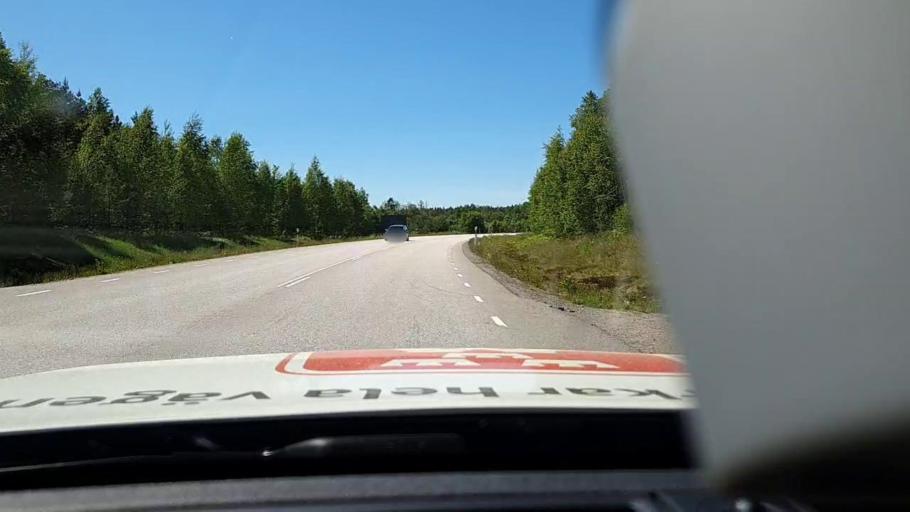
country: SE
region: Uppsala
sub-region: Osthammars Kommun
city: Bjorklinge
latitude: 60.0090
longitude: 17.6202
